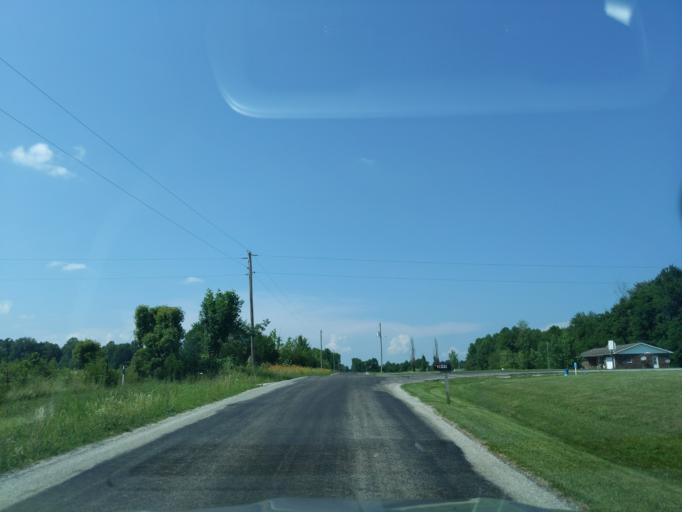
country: US
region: Indiana
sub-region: Ripley County
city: Osgood
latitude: 39.1183
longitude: -85.3426
